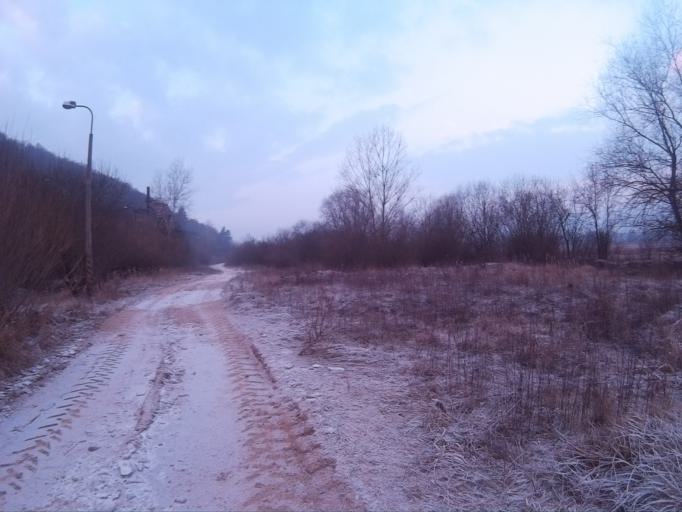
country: HU
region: Borsod-Abauj-Zemplen
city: Szendro
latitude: 48.5225
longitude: 20.7513
